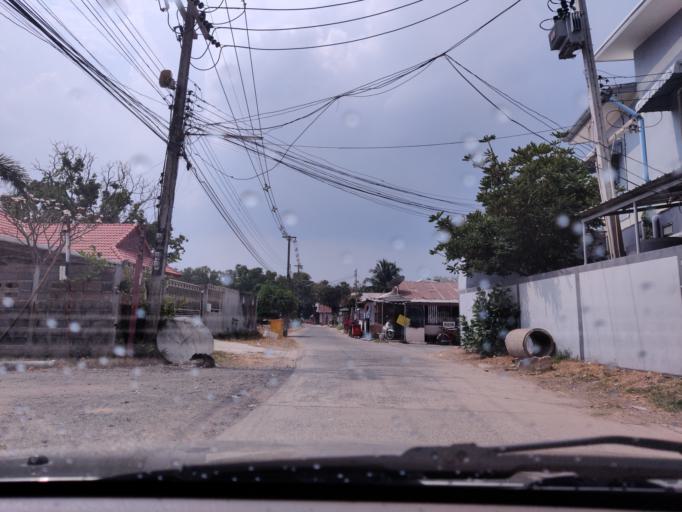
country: TH
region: Sisaket
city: Si Sa Ket
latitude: 15.1025
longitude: 104.3535
